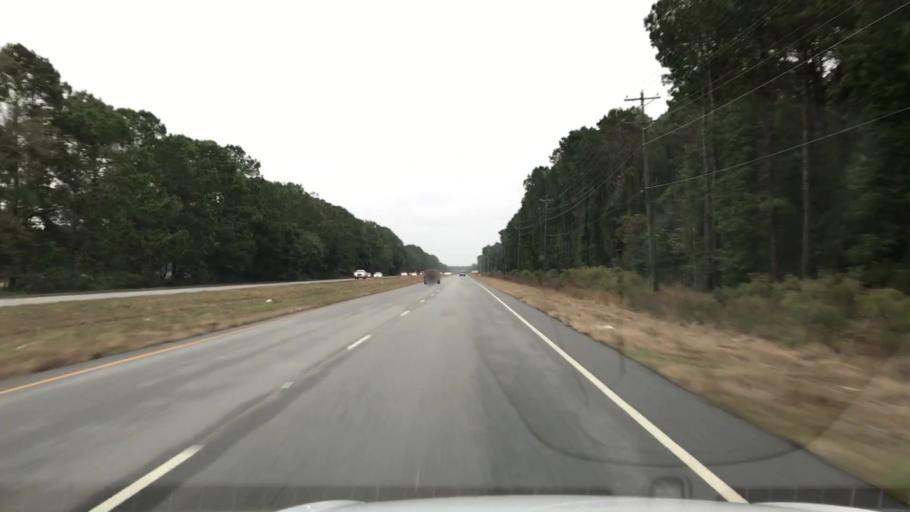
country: US
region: South Carolina
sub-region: Charleston County
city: Isle of Palms
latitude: 32.9031
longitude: -79.7287
